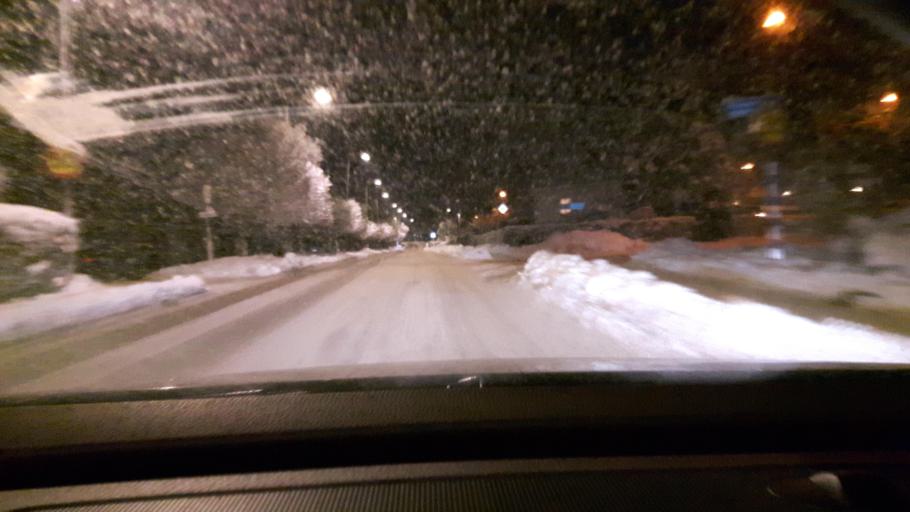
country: SE
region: Vaestra Goetaland
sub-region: Goteborg
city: Majorna
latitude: 57.6642
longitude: 11.8750
